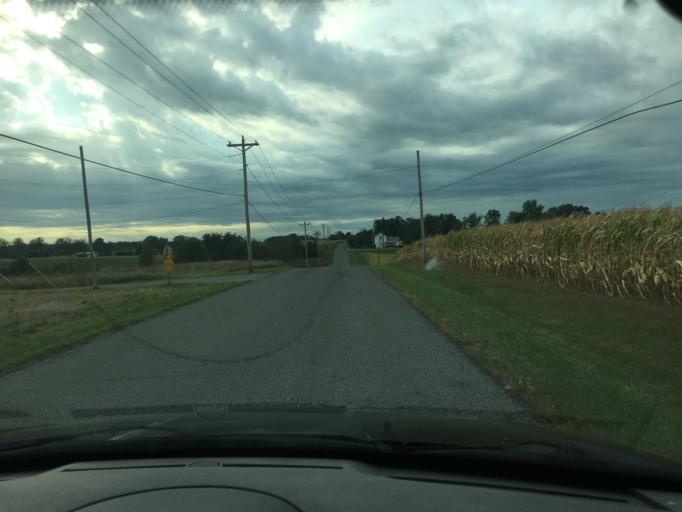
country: US
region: Ohio
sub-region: Logan County
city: Bellefontaine
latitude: 40.3338
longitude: -83.7916
